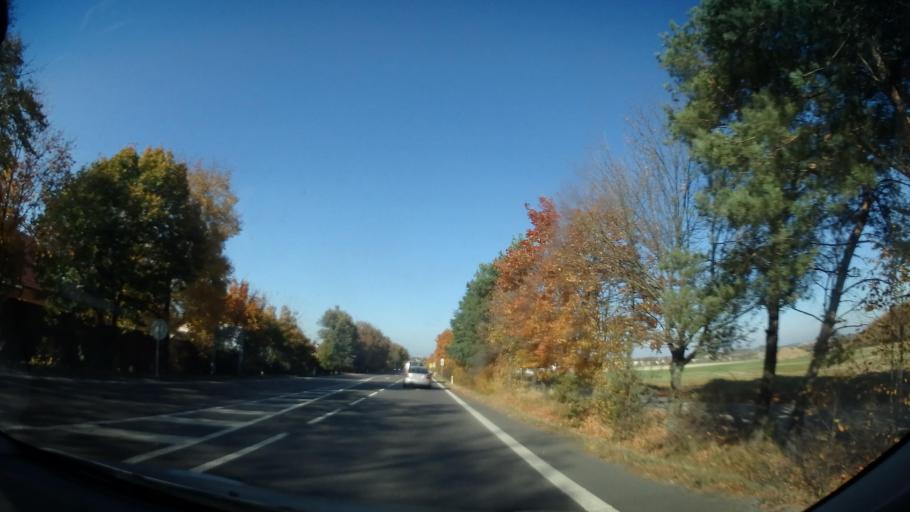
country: CZ
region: Pardubicky
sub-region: Okres Chrudim
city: Slatinany
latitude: 49.9080
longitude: 15.8204
